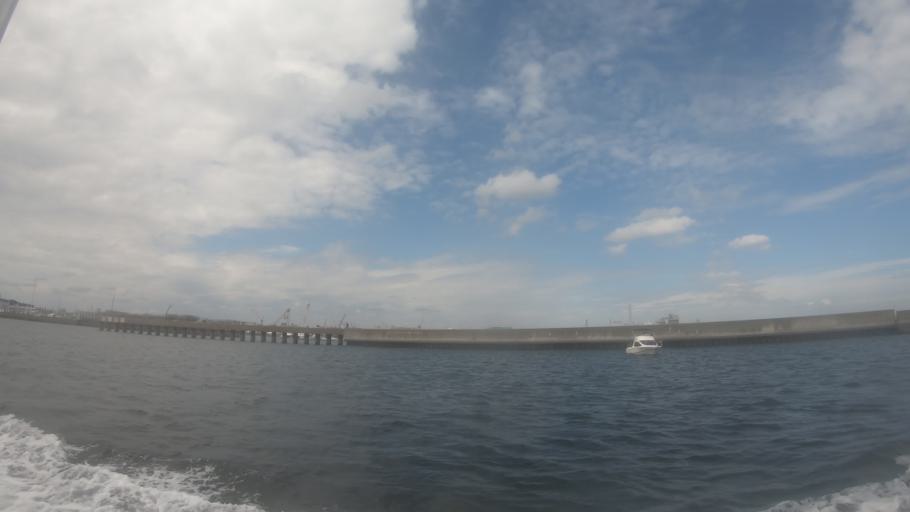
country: JP
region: Kanagawa
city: Yokohama
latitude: 35.3787
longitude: 139.6552
